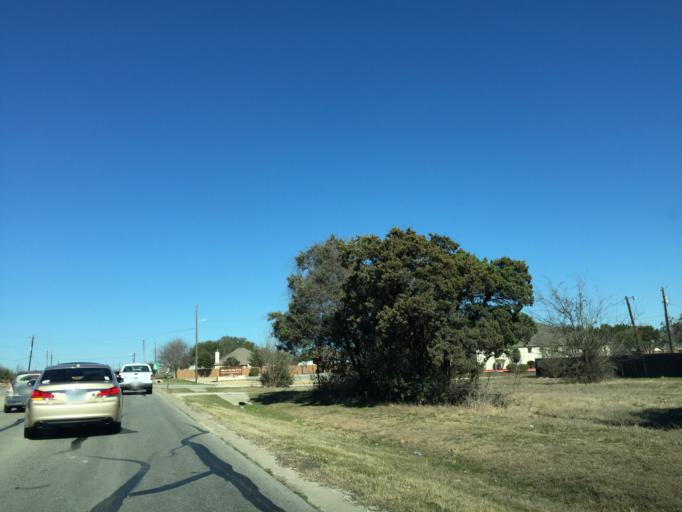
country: US
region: Texas
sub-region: Williamson County
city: Leander
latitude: 30.5585
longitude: -97.8604
